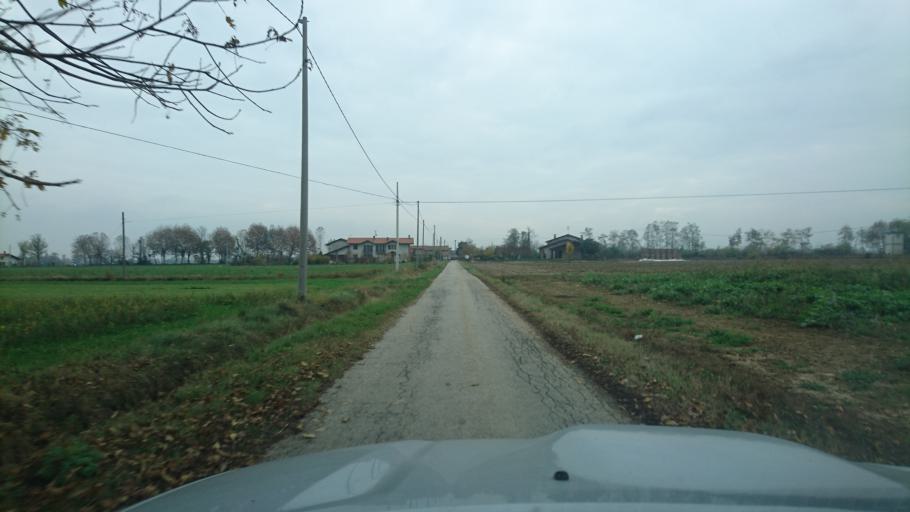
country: IT
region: Piedmont
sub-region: Provincia di Cuneo
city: Cuneo
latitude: 44.4085
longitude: 7.5957
